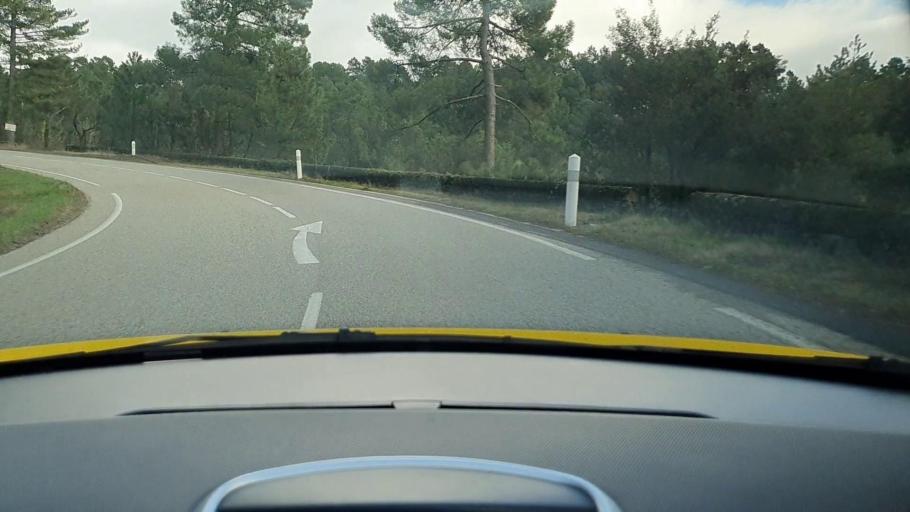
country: FR
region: Languedoc-Roussillon
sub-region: Departement du Gard
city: Branoux-les-Taillades
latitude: 44.2838
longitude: 3.9927
